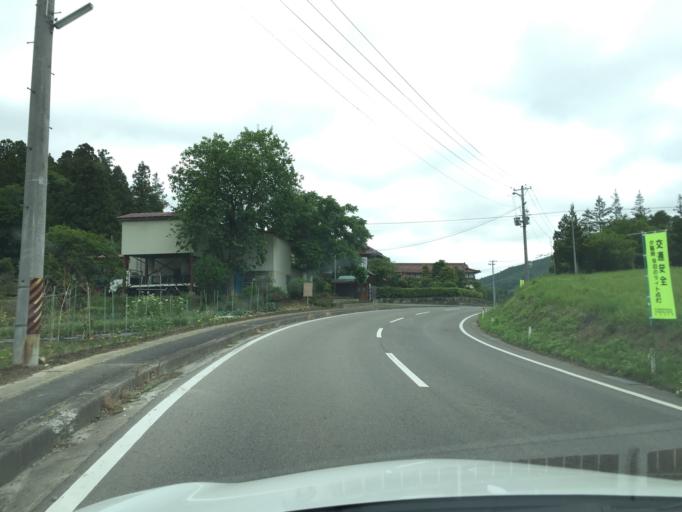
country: JP
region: Fukushima
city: Funehikimachi-funehiki
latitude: 37.4139
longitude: 140.5464
